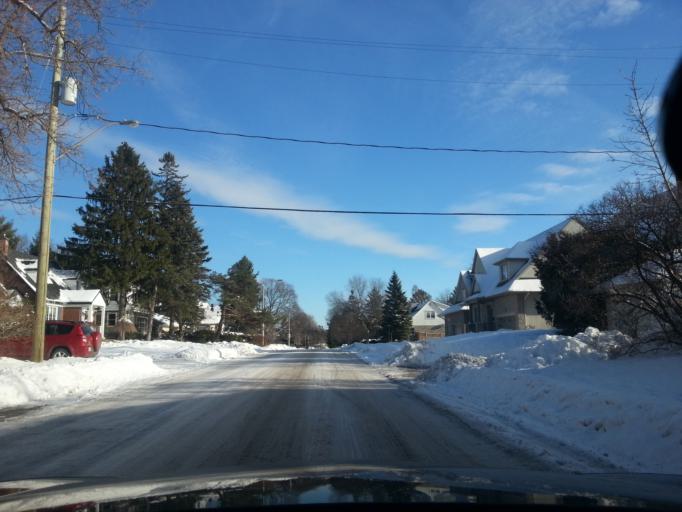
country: CA
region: Ontario
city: Ottawa
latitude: 45.3911
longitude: -75.6618
